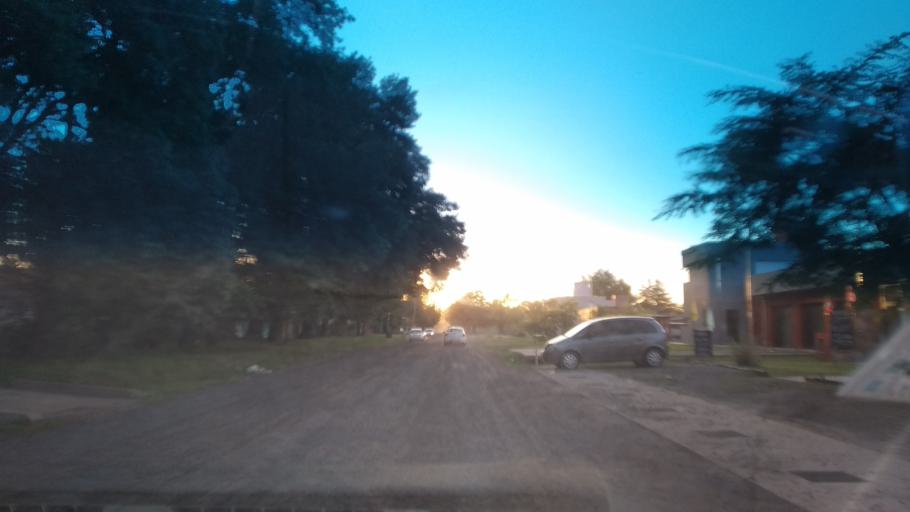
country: AR
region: Santa Fe
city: Funes
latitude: -32.9106
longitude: -60.8026
